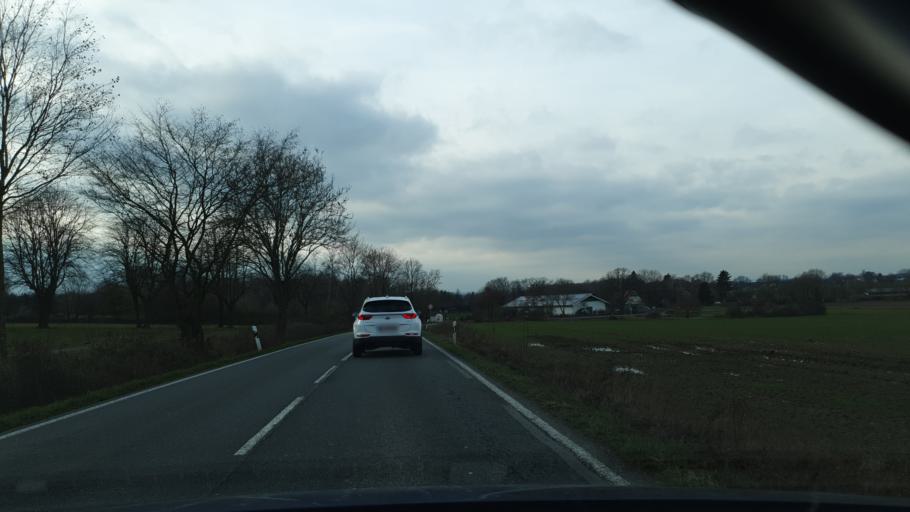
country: DE
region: North Rhine-Westphalia
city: Spenge
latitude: 52.1133
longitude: 8.5002
